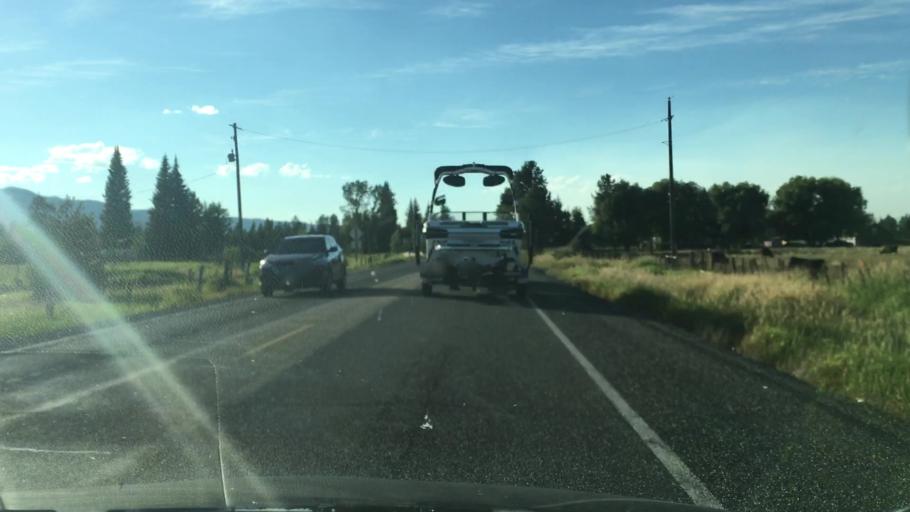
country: US
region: Idaho
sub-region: Valley County
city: McCall
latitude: 44.7233
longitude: -116.0702
